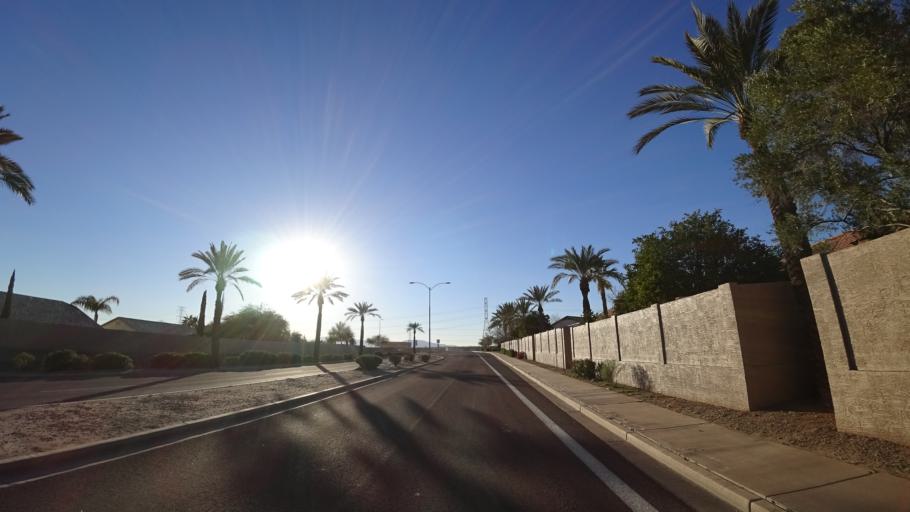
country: US
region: Arizona
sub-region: Maricopa County
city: Sun City West
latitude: 33.6672
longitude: -112.2972
